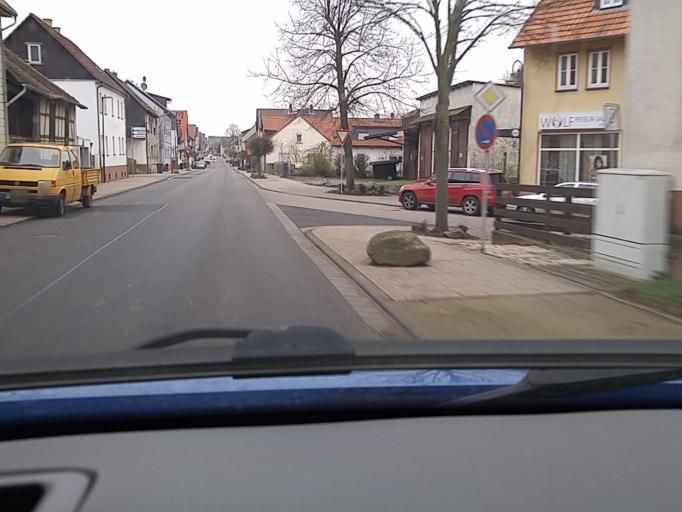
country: DE
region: Hesse
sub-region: Regierungsbezirk Darmstadt
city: Echzell
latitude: 50.3848
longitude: 8.8832
